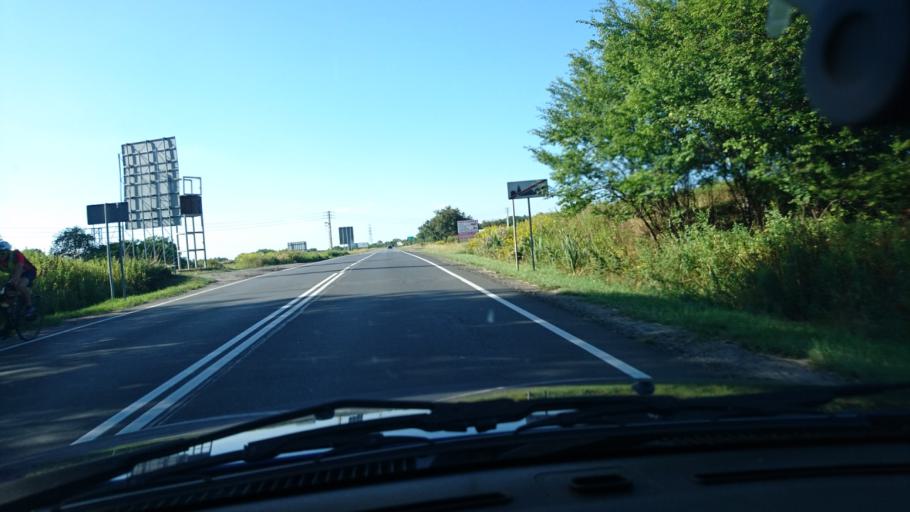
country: PL
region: Silesian Voivodeship
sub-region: Powiat gliwicki
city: Pyskowice
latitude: 50.3691
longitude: 18.6364
